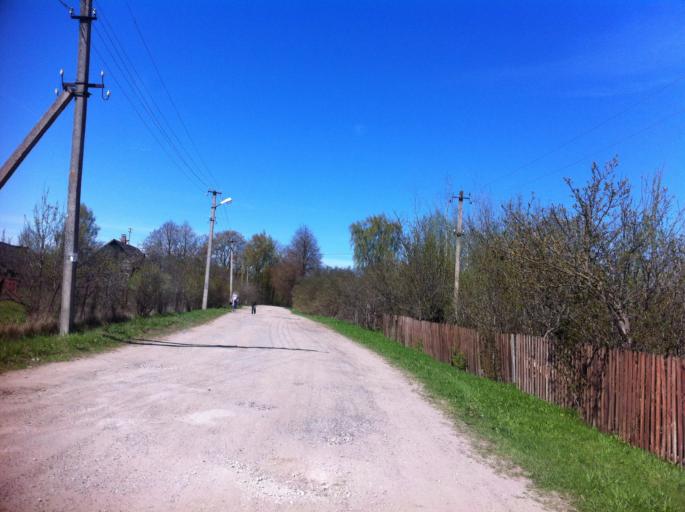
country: RU
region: Pskov
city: Izborsk
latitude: 57.7780
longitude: 27.9651
